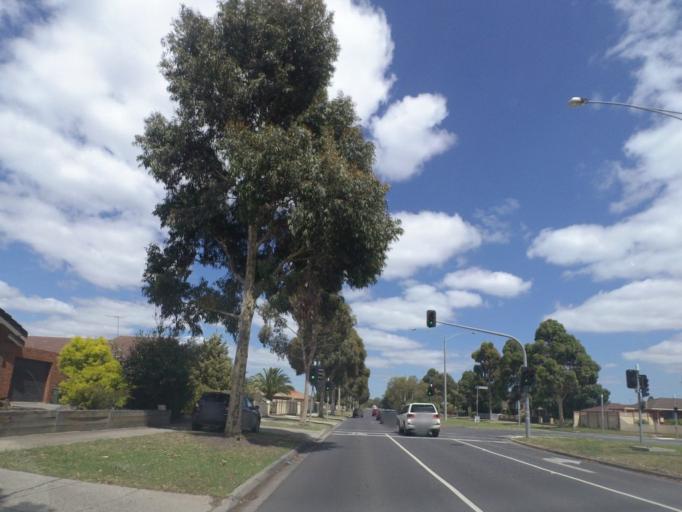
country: AU
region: Victoria
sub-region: Whittlesea
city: Epping
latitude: -37.6626
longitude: 145.0477
